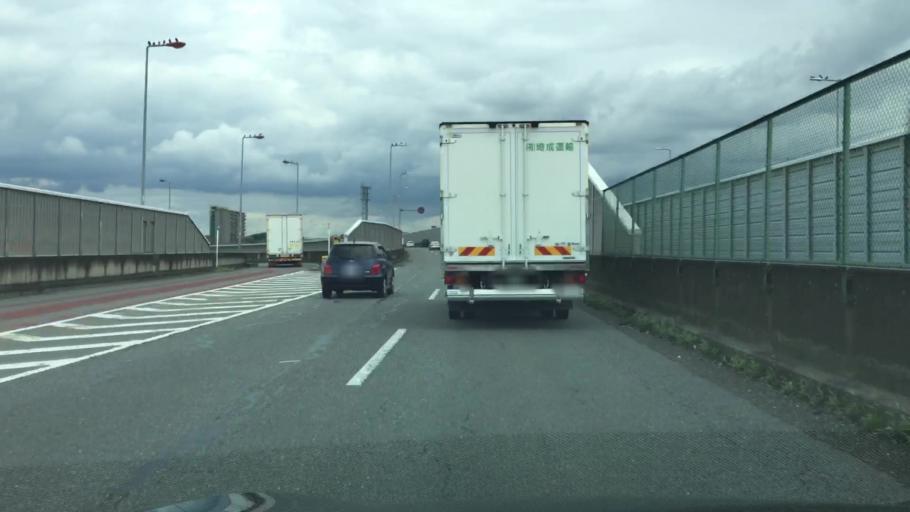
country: JP
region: Saitama
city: Kamifukuoka
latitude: 35.9185
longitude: 139.5564
